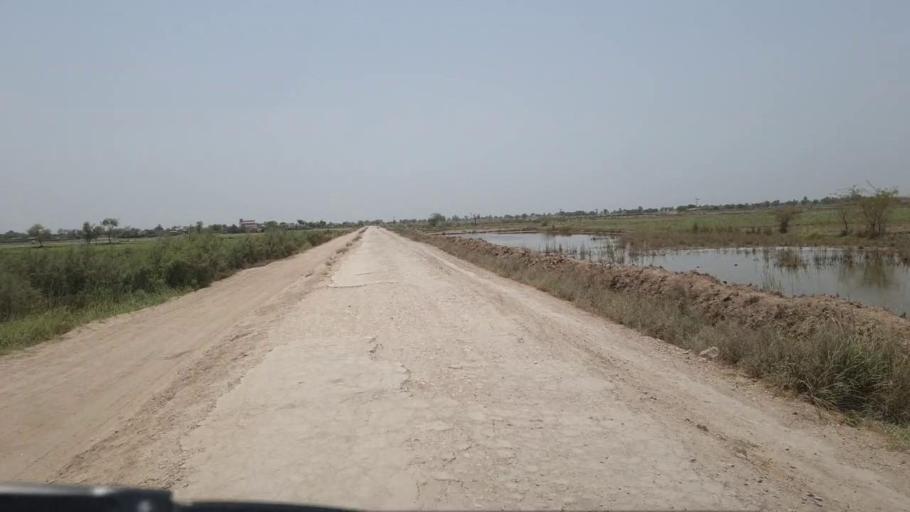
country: PK
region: Sindh
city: Daur
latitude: 26.4612
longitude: 68.1460
